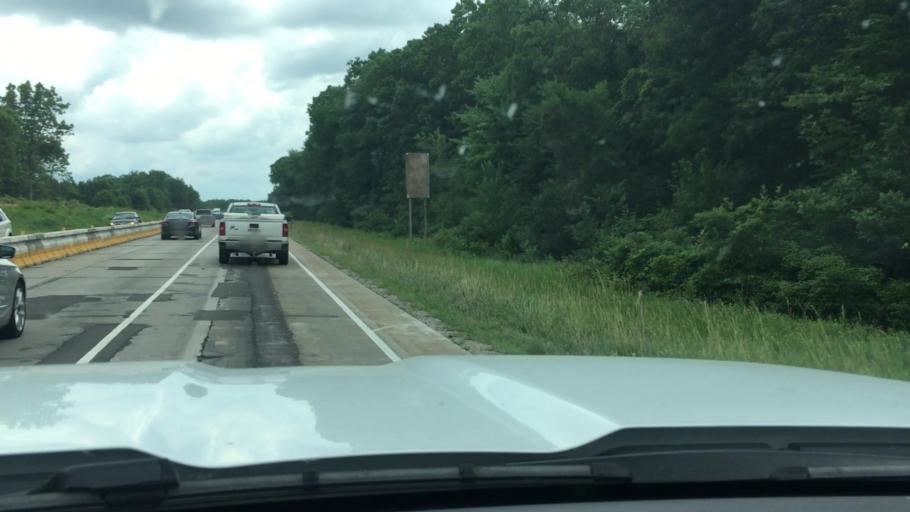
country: US
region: Michigan
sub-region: Kent County
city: Rockford
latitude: 43.1275
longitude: -85.5996
